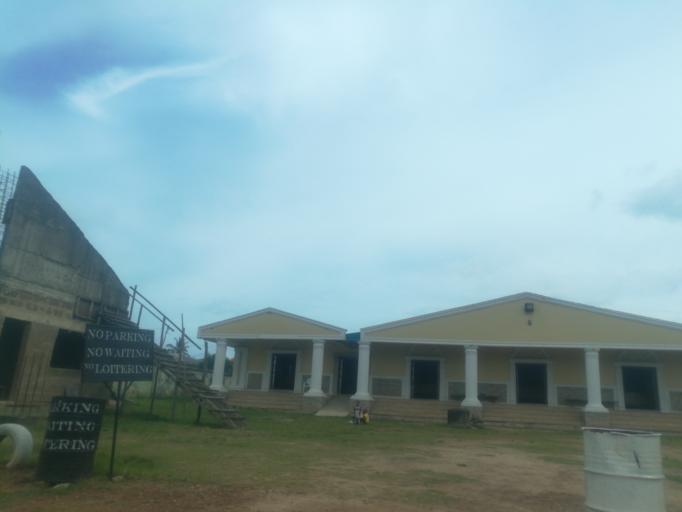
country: NG
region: Oyo
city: Ibadan
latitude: 7.3675
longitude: 3.9706
